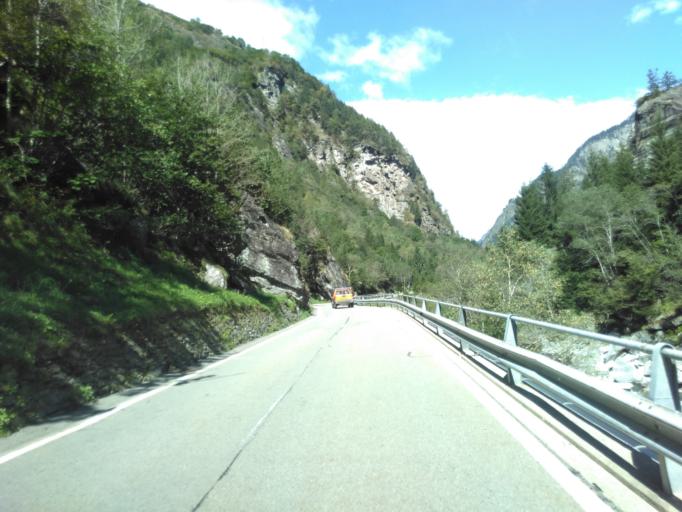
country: CH
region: Grisons
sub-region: Moesa District
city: Arvigo
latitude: 46.3125
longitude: 9.1156
